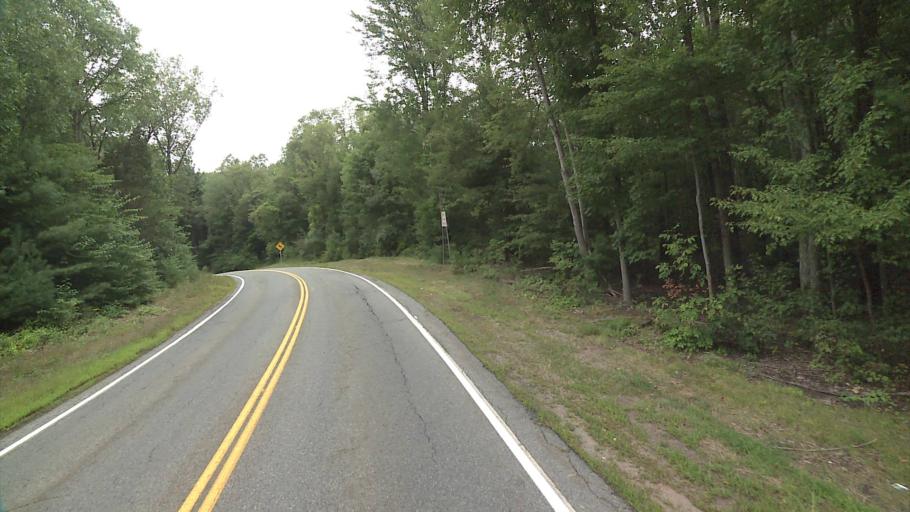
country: US
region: Connecticut
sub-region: Hartford County
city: Manchester
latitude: 41.7863
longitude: -72.4668
